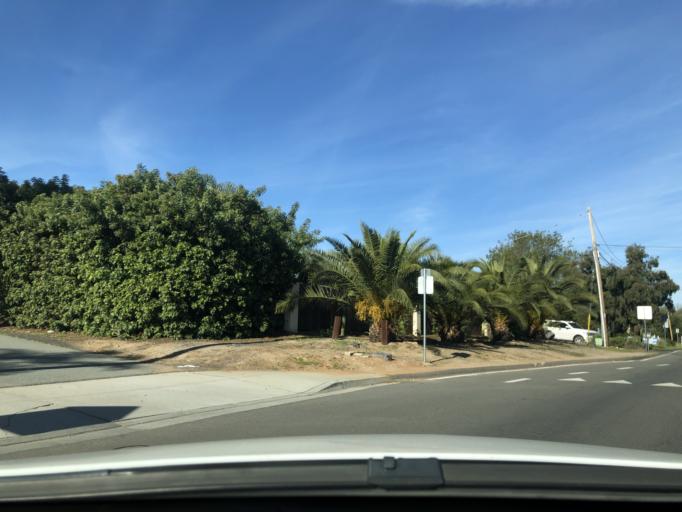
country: US
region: California
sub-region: San Diego County
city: Escondido
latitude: 33.0963
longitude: -117.0834
